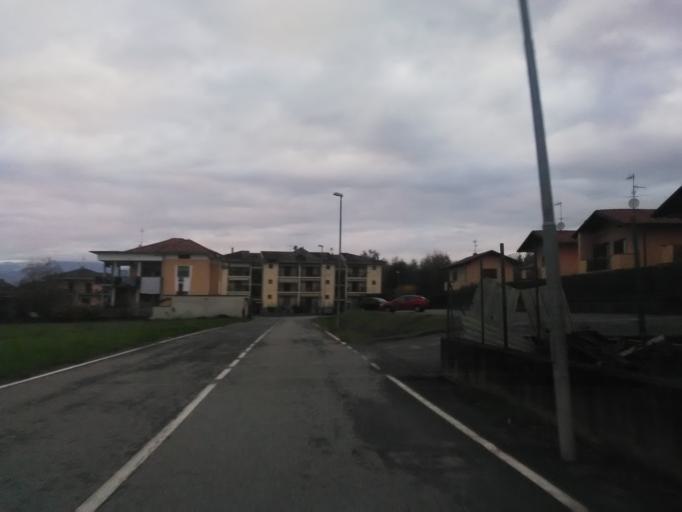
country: IT
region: Piedmont
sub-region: Provincia di Novara
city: Prato Sesia
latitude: 45.6530
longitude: 8.3744
